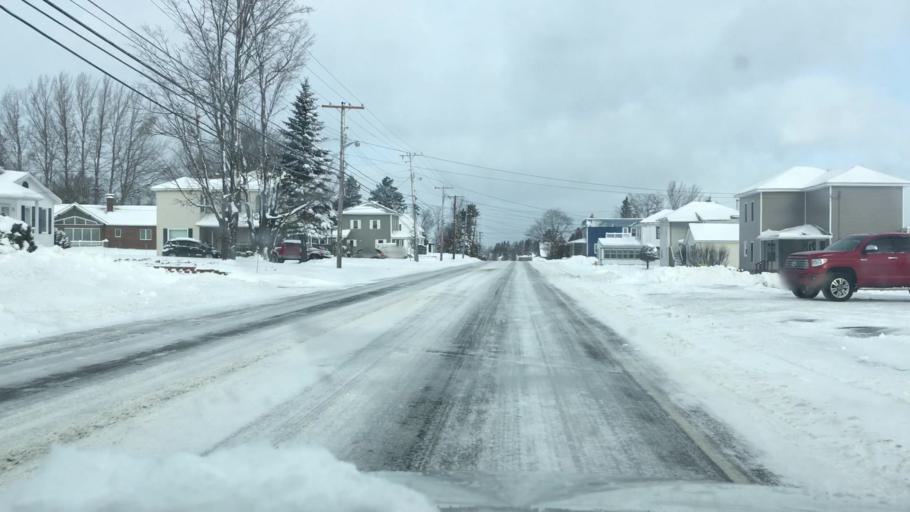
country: US
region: Maine
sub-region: Aroostook County
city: Van Buren
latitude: 47.1668
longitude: -67.9429
